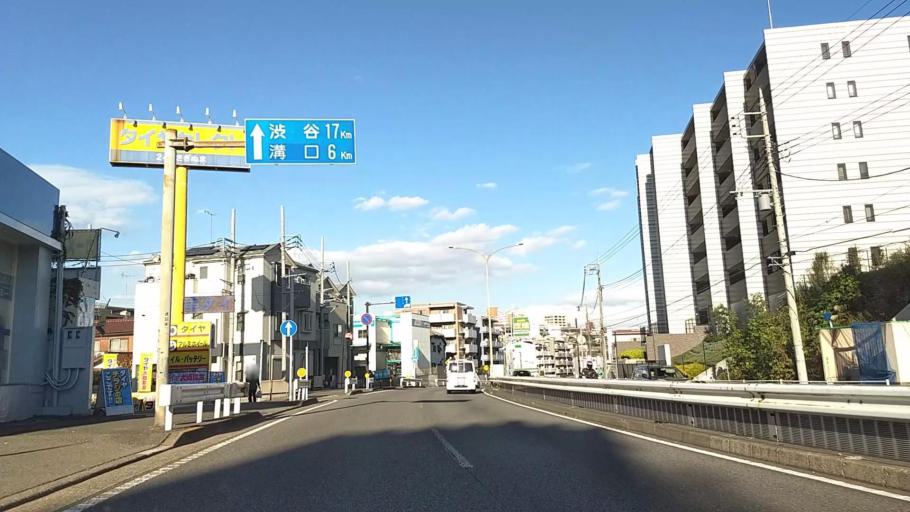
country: JP
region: Tokyo
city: Chofugaoka
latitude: 35.5730
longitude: 139.5685
